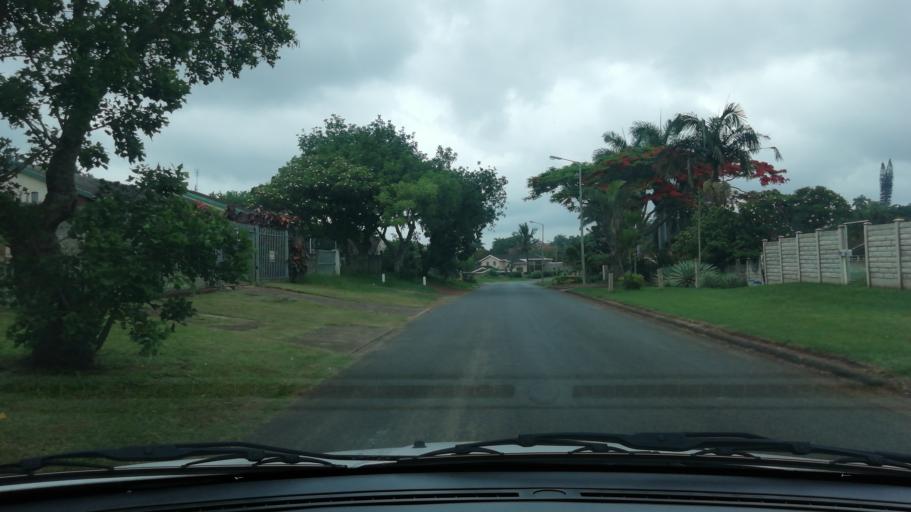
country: ZA
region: KwaZulu-Natal
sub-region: uThungulu District Municipality
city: Empangeni
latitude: -28.7620
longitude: 31.9003
